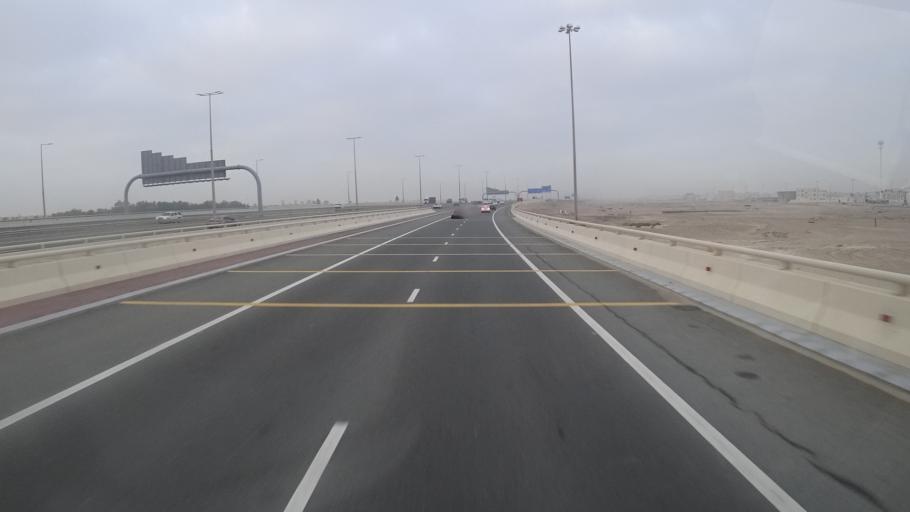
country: AE
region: Abu Dhabi
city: Abu Dhabi
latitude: 24.3030
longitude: 54.5948
